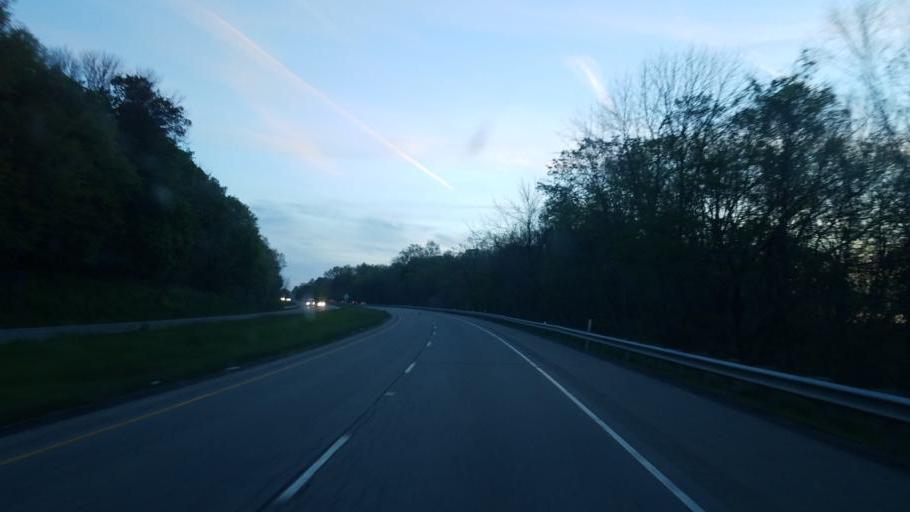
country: US
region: Ohio
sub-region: Richland County
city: Mansfield
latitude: 40.7114
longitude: -82.5042
